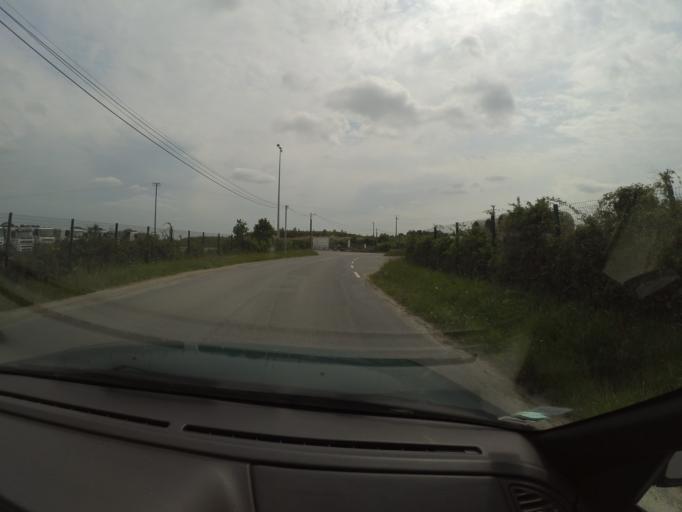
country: FR
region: Pays de la Loire
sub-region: Departement de la Loire-Atlantique
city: Gorges
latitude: 47.1013
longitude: -1.3164
